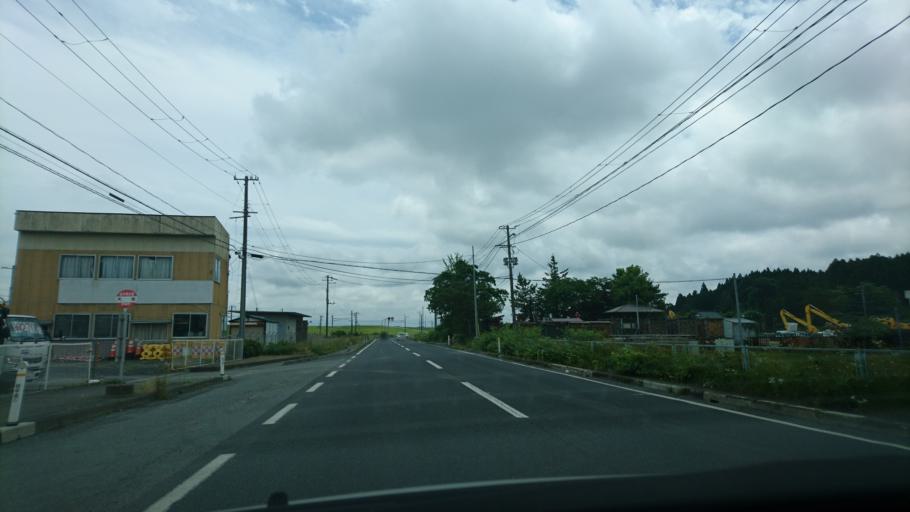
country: JP
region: Iwate
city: Ichinoseki
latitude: 38.9629
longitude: 141.1264
